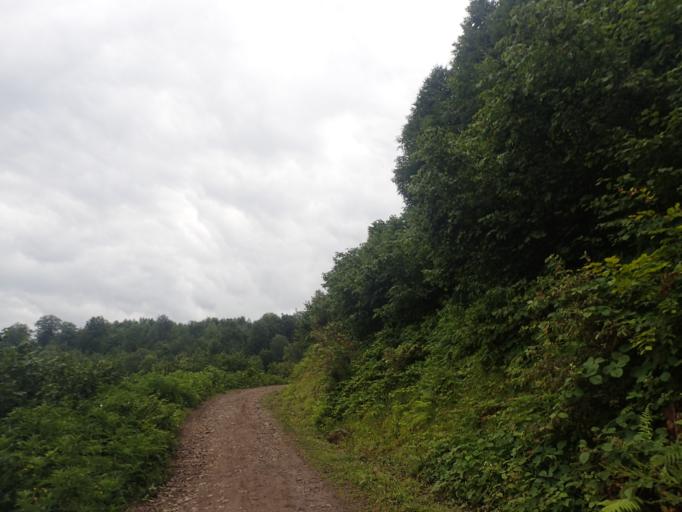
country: TR
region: Ordu
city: Akkus
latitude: 40.8055
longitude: 37.0881
